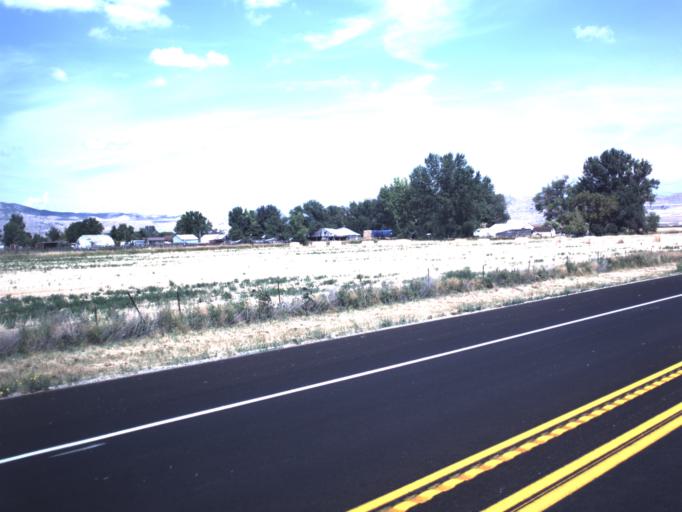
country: US
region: Utah
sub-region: Box Elder County
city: Garland
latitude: 41.7854
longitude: -112.1289
